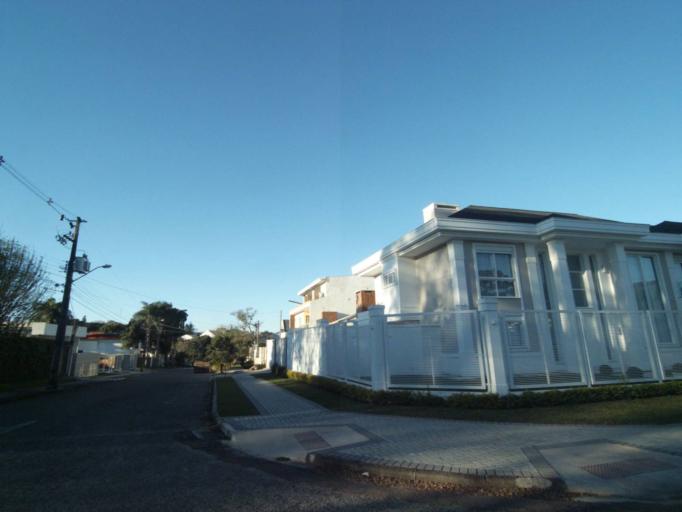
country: BR
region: Parana
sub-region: Curitiba
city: Curitiba
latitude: -25.4170
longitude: -49.2348
